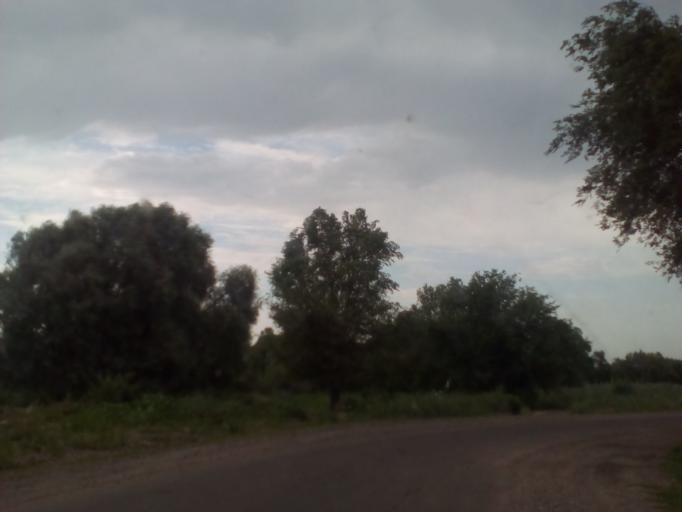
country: KZ
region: Almaty Oblysy
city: Burunday
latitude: 43.1630
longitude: 76.3812
